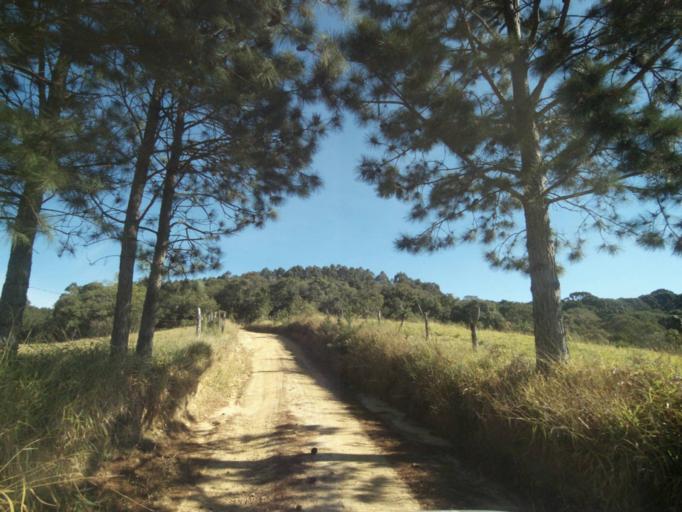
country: BR
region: Parana
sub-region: Tibagi
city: Tibagi
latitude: -24.5512
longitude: -50.4719
